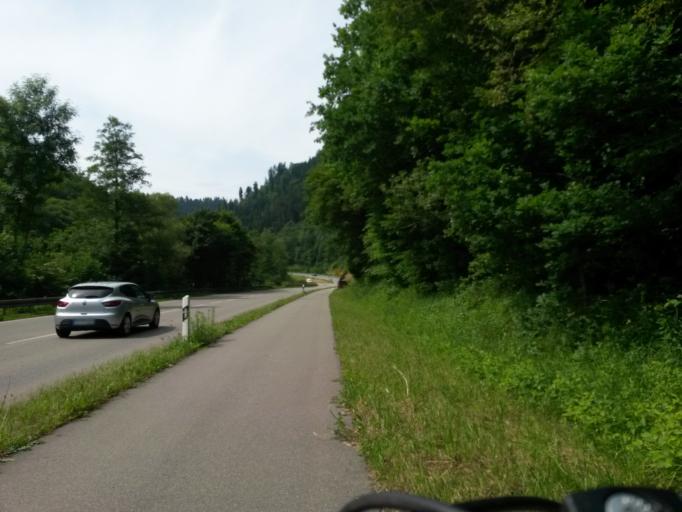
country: DE
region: Baden-Wuerttemberg
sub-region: Karlsruhe Region
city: Calw
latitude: 48.6852
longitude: 8.7289
